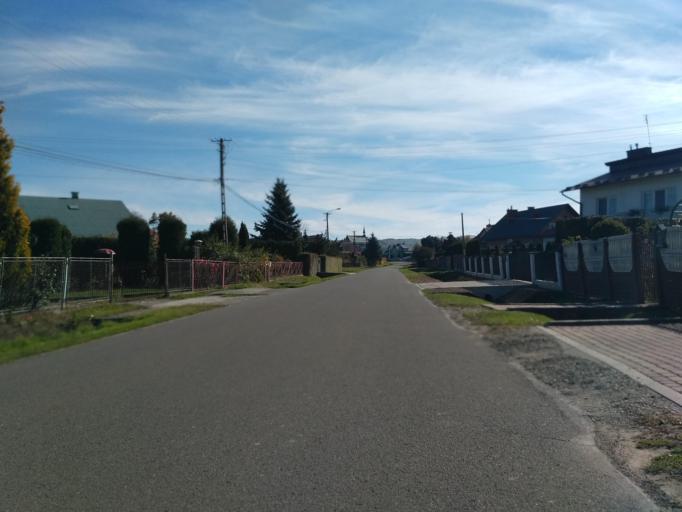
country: PL
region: Subcarpathian Voivodeship
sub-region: Powiat ropczycko-sedziszowski
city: Iwierzyce
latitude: 50.0627
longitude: 21.7815
